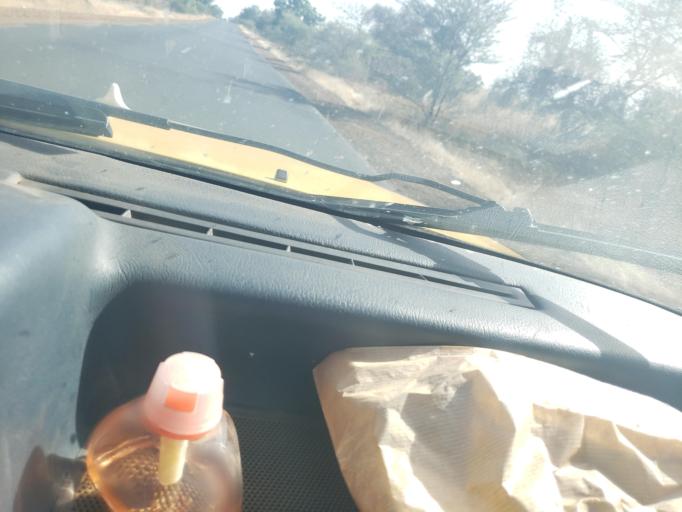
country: SN
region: Louga
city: Louga
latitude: 15.6549
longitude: -16.2562
